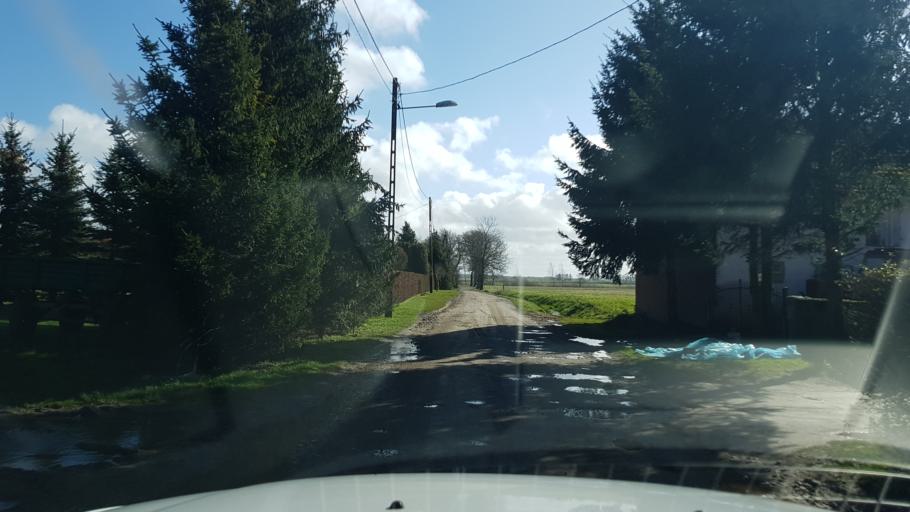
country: PL
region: West Pomeranian Voivodeship
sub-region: Powiat slawienski
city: Slawno
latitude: 54.3640
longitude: 16.5815
